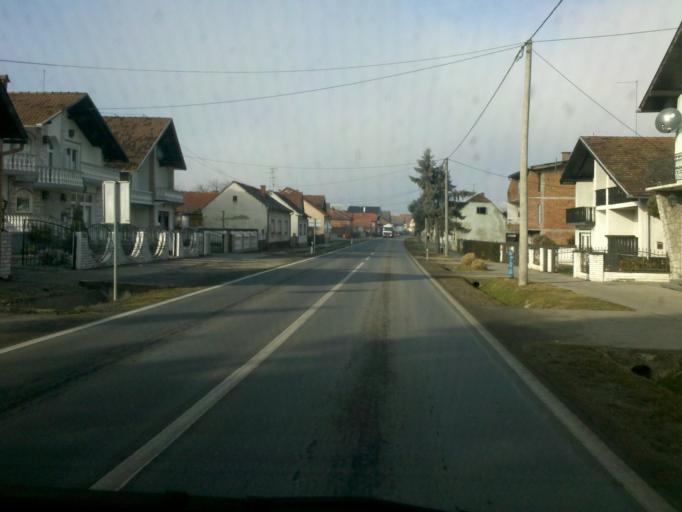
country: HR
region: Virovitick-Podravska
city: Pitomaca
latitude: 45.9533
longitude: 17.2326
